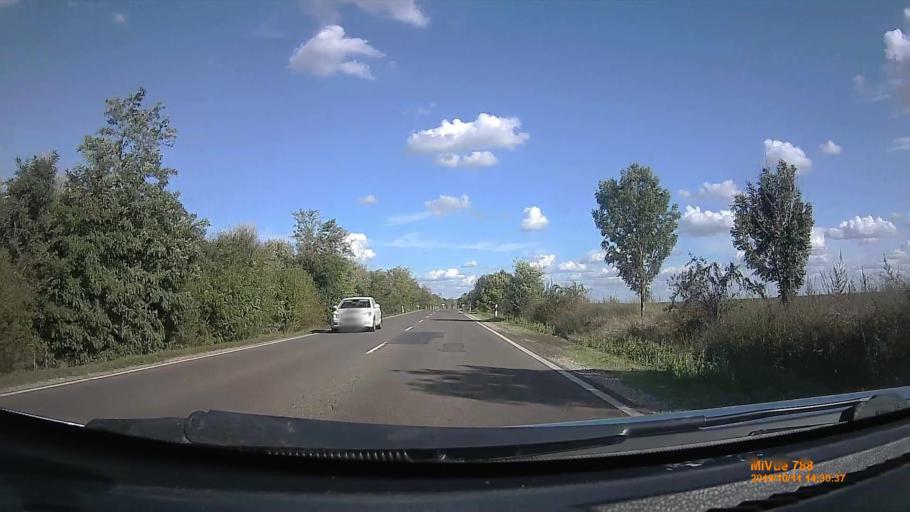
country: HU
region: Hajdu-Bihar
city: Balmazujvaros
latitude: 47.5607
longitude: 21.4039
